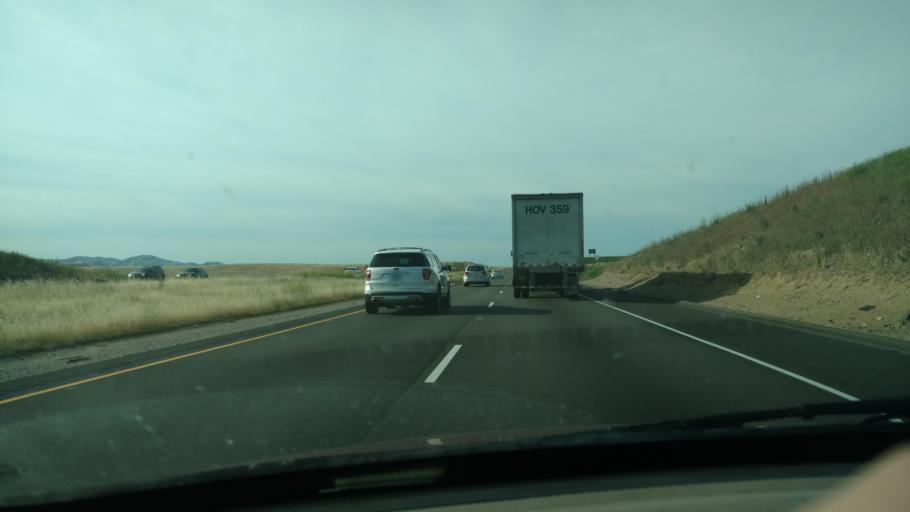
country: US
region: California
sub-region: Stanislaus County
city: Newman
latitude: 37.3586
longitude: -121.1206
